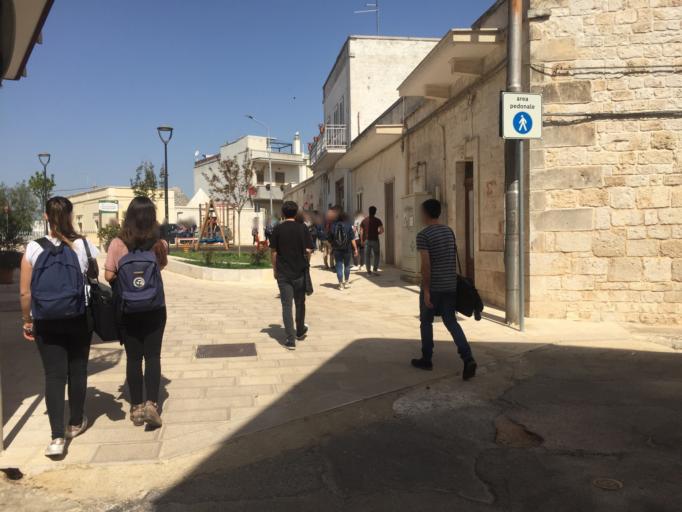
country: IT
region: Apulia
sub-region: Provincia di Brindisi
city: Casalini
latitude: 40.7361
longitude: 17.4713
